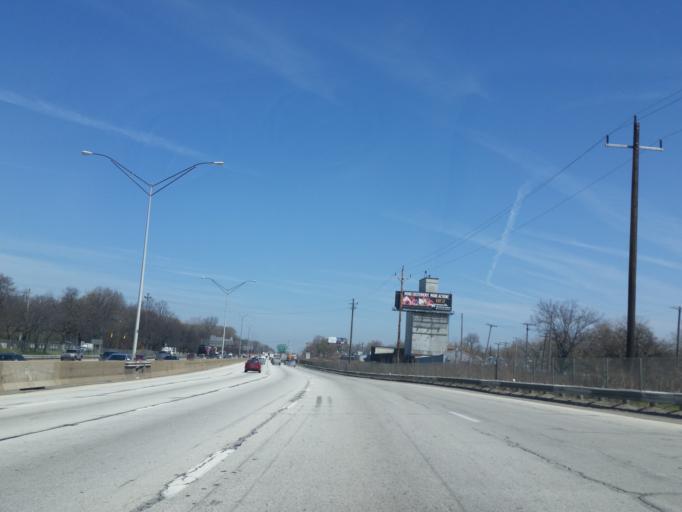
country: US
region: Ohio
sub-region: Cuyahoga County
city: Bratenahl
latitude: 41.5397
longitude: -81.6272
